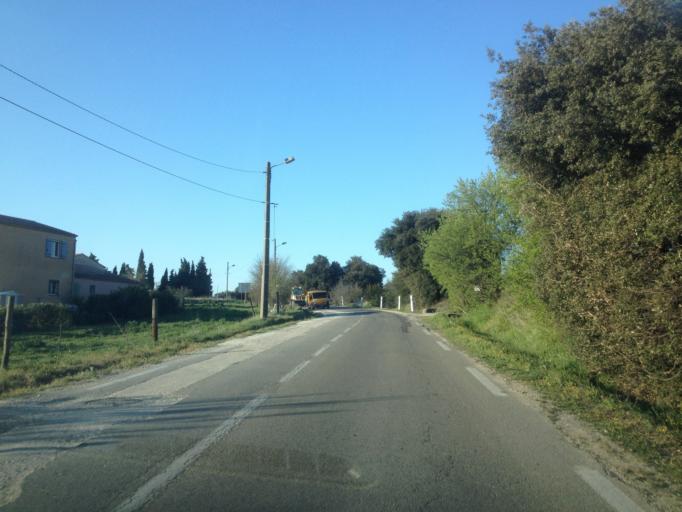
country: FR
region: Provence-Alpes-Cote d'Azur
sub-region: Departement du Vaucluse
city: Orange
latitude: 44.1206
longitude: 4.8189
